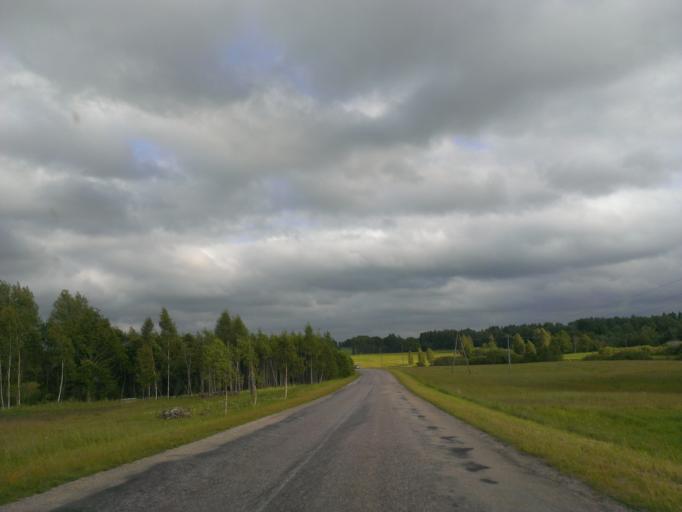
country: LV
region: Aizpute
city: Aizpute
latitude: 56.7139
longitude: 21.7622
